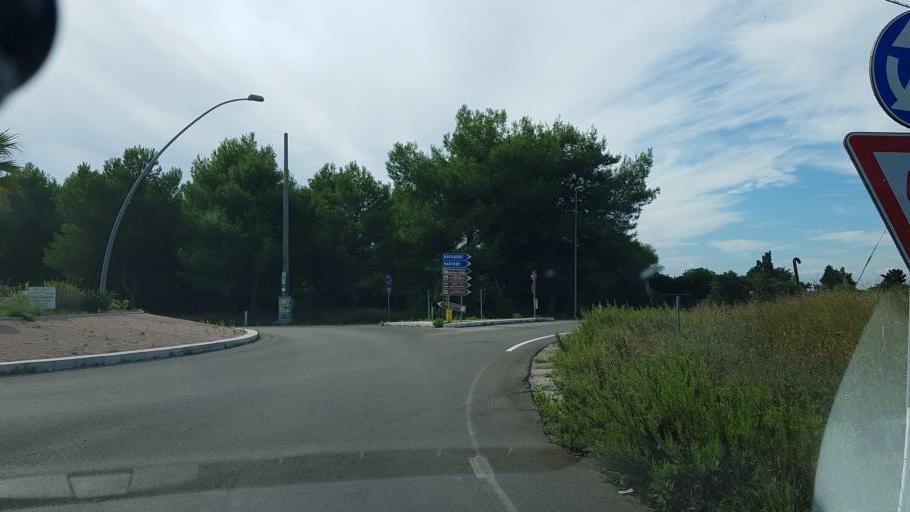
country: IT
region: Apulia
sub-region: Provincia di Lecce
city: Borgagne
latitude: 40.2541
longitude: 18.4385
